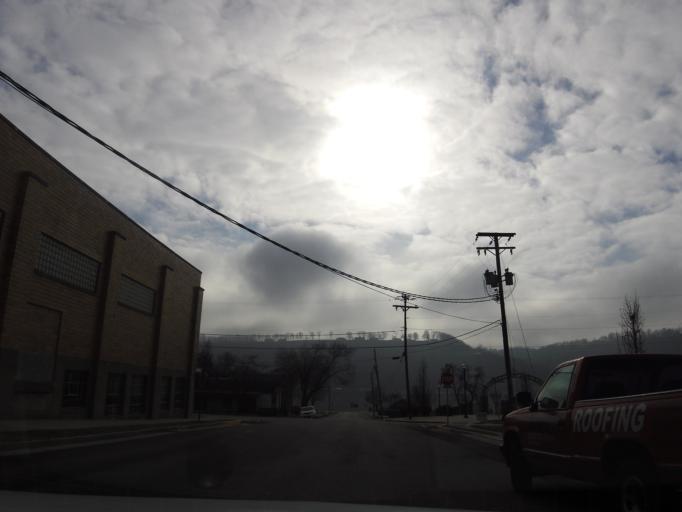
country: US
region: Indiana
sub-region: Jefferson County
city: Madison
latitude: 38.7349
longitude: -85.3802
